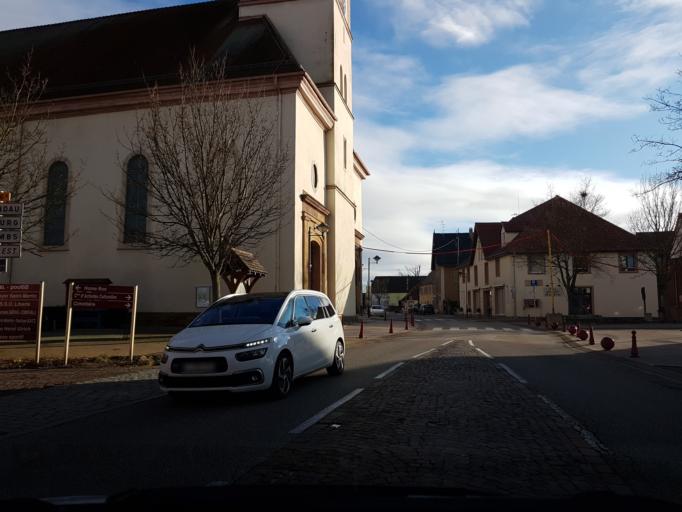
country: FR
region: Alsace
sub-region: Departement du Haut-Rhin
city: Habsheim
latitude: 47.7288
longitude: 7.4167
